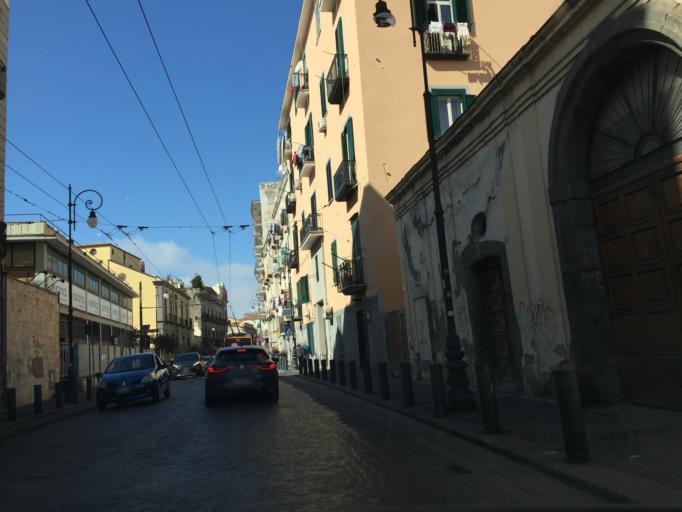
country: IT
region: Campania
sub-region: Provincia di Napoli
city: Portici
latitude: 40.8211
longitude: 14.3265
